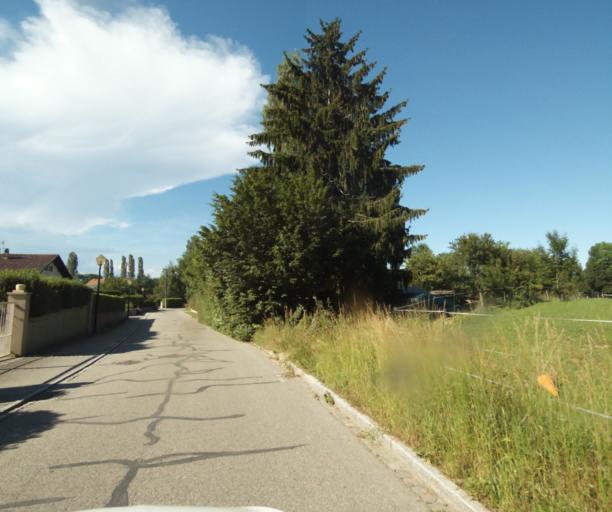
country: FR
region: Rhone-Alpes
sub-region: Departement de la Haute-Savoie
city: Massongy
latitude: 46.3245
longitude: 6.3264
